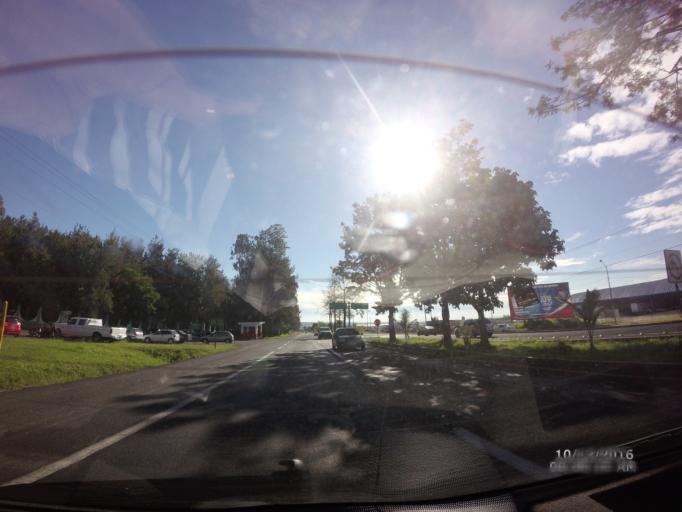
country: TR
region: Sivas
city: Sivas
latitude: 39.6813
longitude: 37.0502
